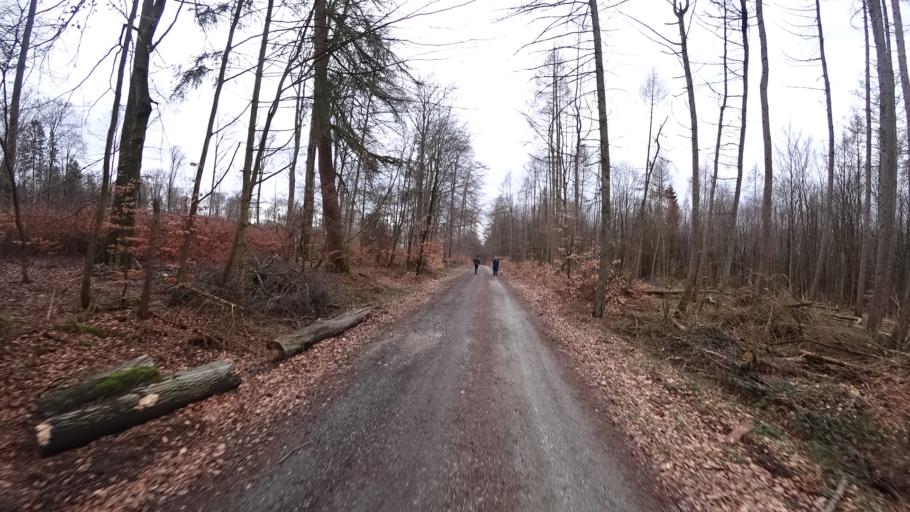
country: DE
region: Rheinland-Pfalz
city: Hundsdorf
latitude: 50.4411
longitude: 7.7139
